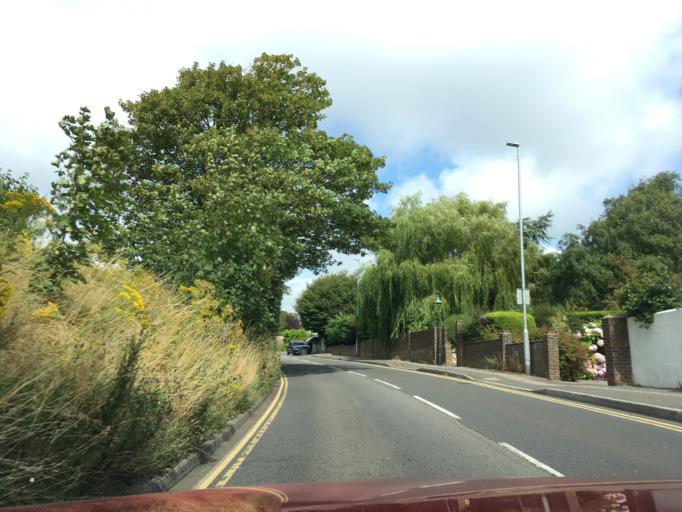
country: GB
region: England
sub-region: Brighton and Hove
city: Rottingdean
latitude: 50.8312
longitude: -0.0733
